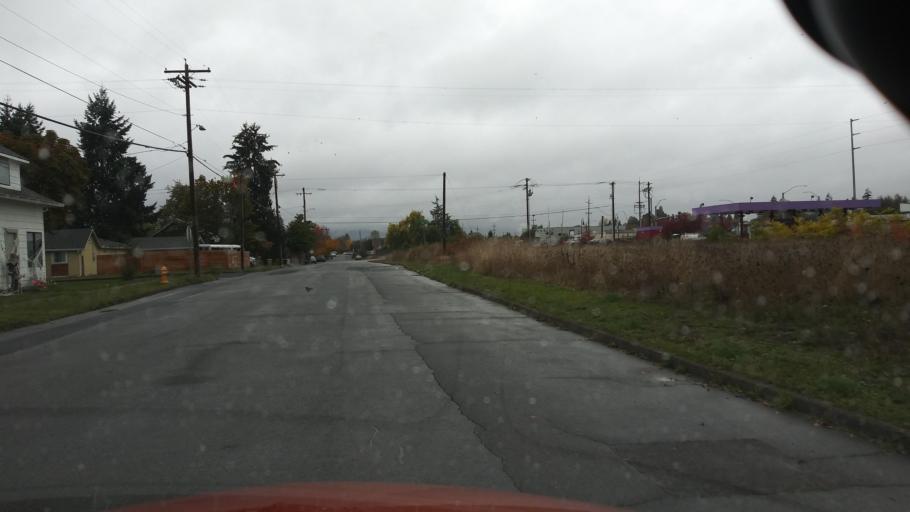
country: US
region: Oregon
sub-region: Washington County
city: Cornelius
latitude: 45.5193
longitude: -123.0576
